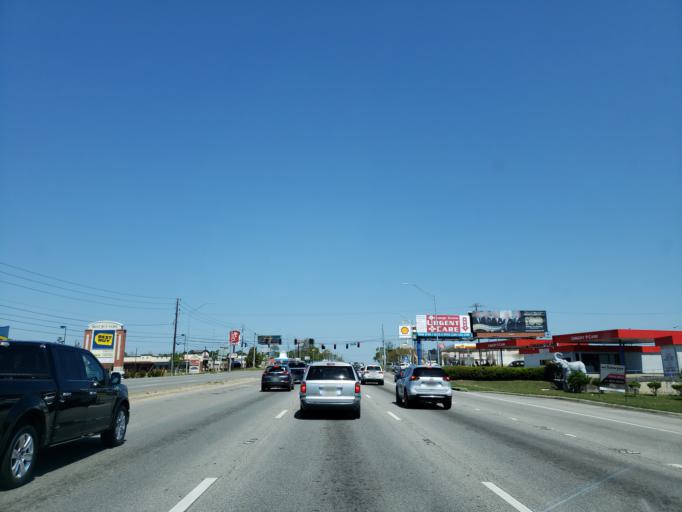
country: US
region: Mississippi
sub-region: Harrison County
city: West Gulfport
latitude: 30.4408
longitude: -89.0979
